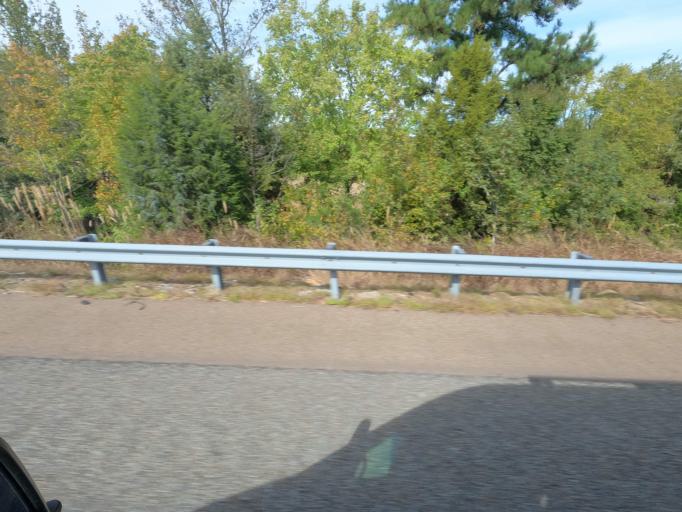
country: US
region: Tennessee
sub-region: Humphreys County
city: New Johnsonville
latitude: 35.8537
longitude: -88.0618
